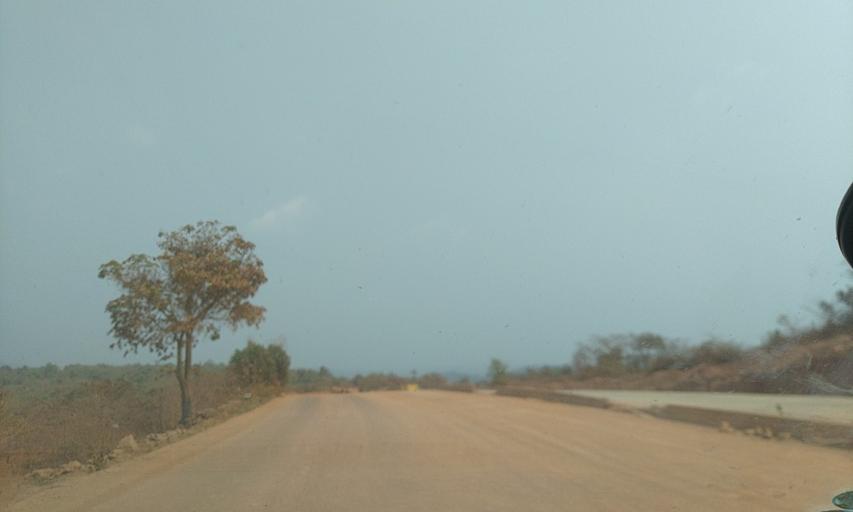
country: IN
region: Goa
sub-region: North Goa
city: Queula
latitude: 15.3506
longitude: 73.9664
